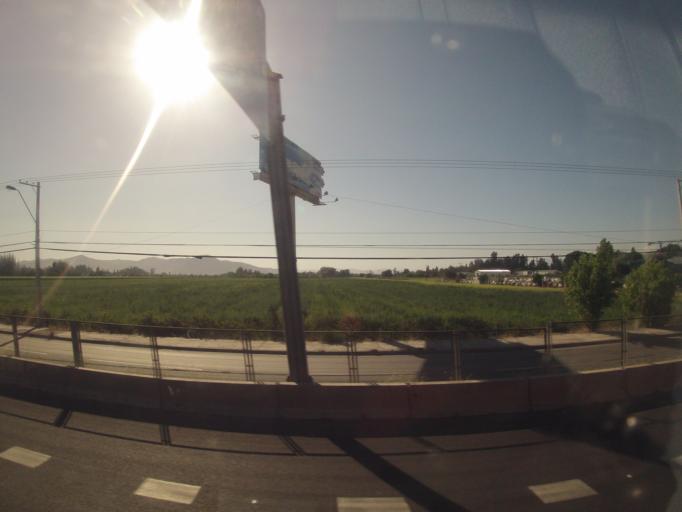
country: CL
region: Santiago Metropolitan
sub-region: Provincia de Maipo
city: San Bernardo
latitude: -33.6607
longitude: -70.7175
